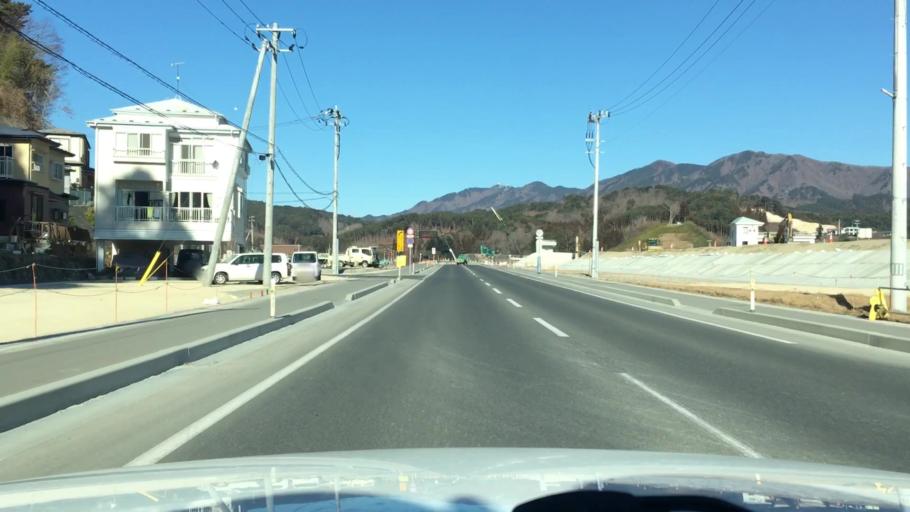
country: JP
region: Iwate
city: Yamada
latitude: 39.4700
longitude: 141.9528
